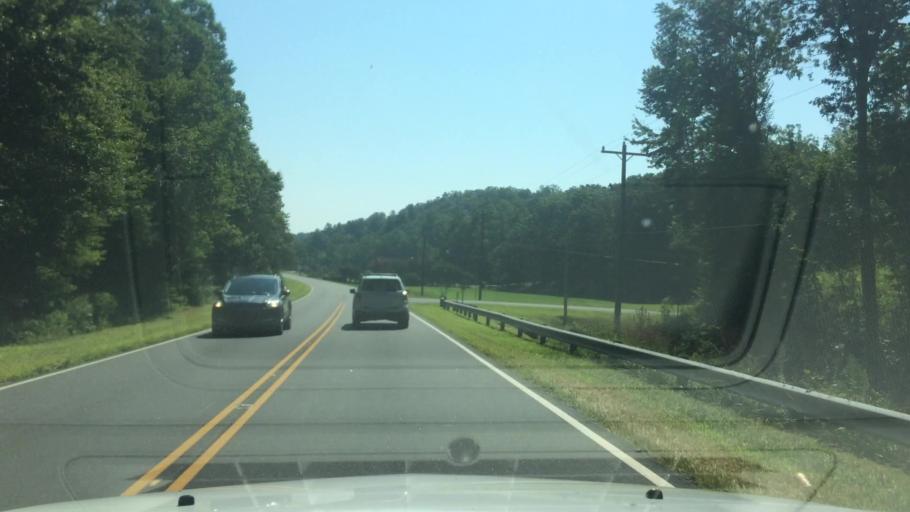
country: US
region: North Carolina
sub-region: Caldwell County
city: Lenoir
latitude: 35.9149
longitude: -81.4723
